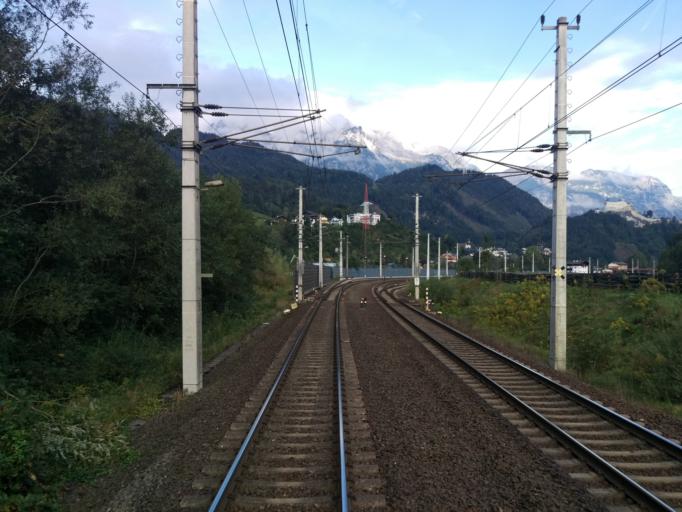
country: AT
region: Salzburg
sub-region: Politischer Bezirk Sankt Johann im Pongau
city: Pfarrwerfen
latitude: 47.4685
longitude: 13.1979
